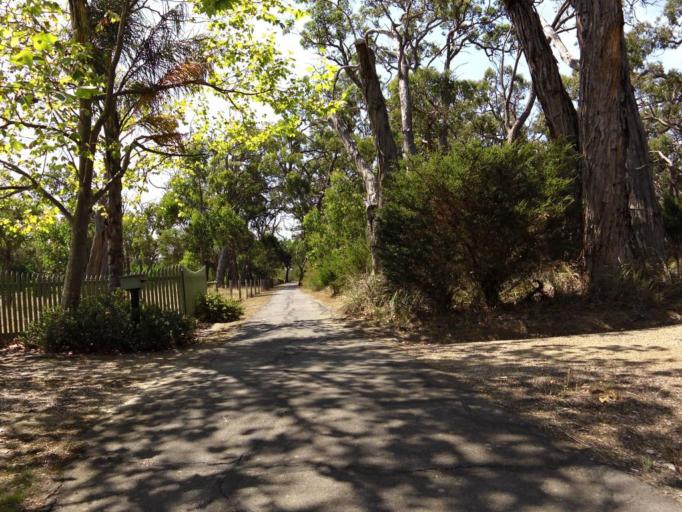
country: AU
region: Victoria
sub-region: Mornington Peninsula
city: Crib Point
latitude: -38.3477
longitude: 145.1697
